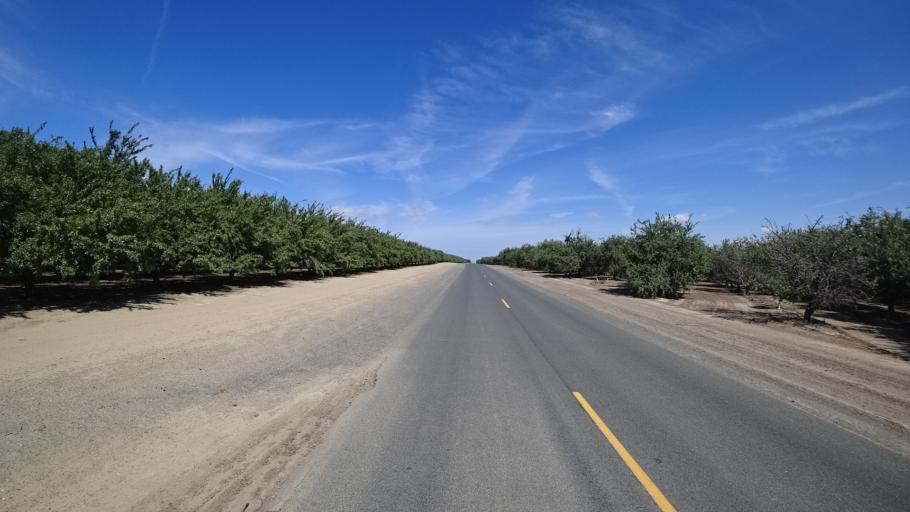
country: US
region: California
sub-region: Kings County
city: Kettleman City
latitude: 35.9731
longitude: -119.9442
